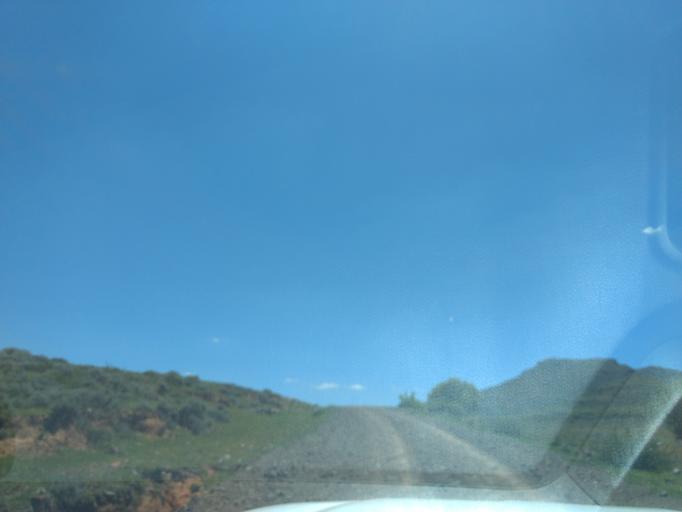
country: LS
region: Maseru
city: Maseru
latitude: -29.4772
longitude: 27.3745
